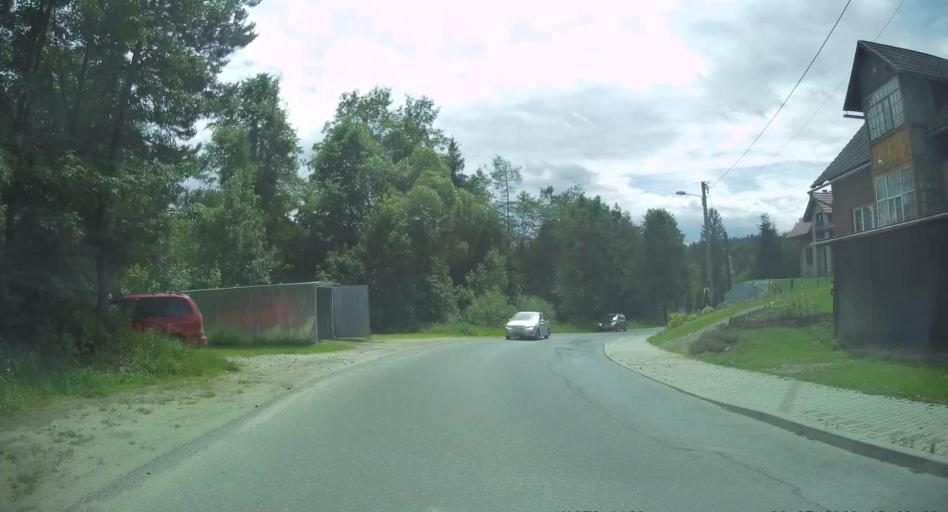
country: PL
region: Lesser Poland Voivodeship
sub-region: Powiat nowosadecki
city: Muszyna
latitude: 49.3770
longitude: 20.8892
